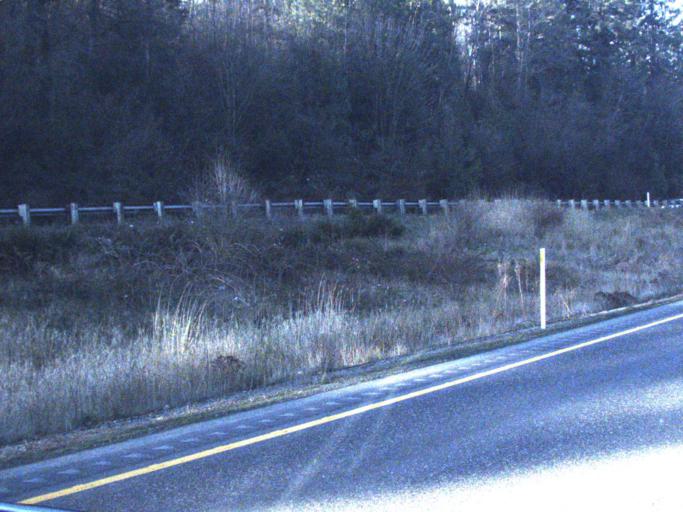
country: US
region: Washington
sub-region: Whatcom County
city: Sudden Valley
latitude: 48.6144
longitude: -122.3520
